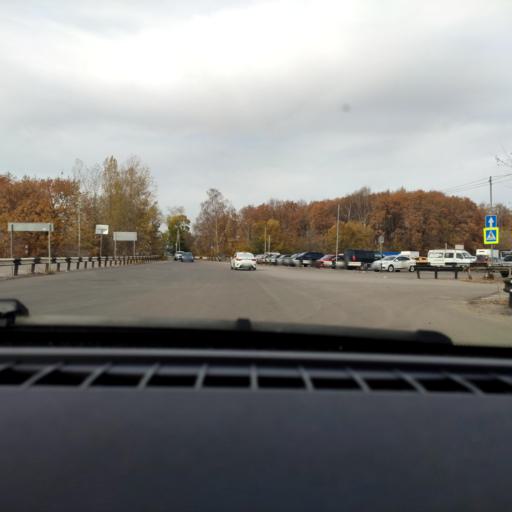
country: RU
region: Voronezj
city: Voronezh
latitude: 51.6673
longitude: 39.2734
